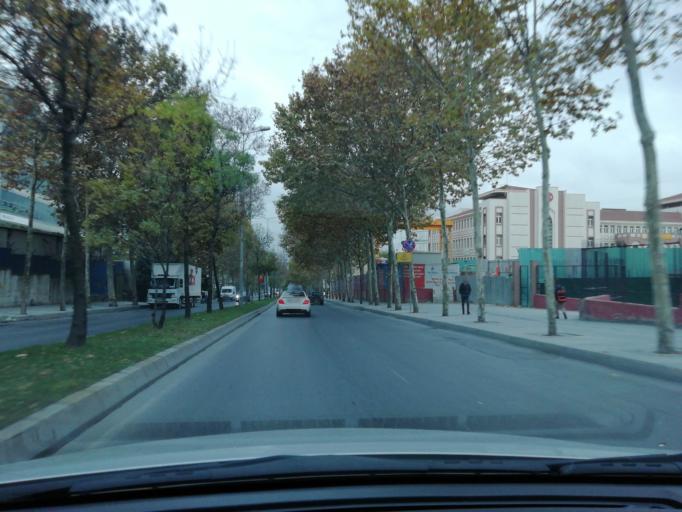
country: TR
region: Istanbul
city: Mahmutbey
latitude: 41.0227
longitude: 28.8215
